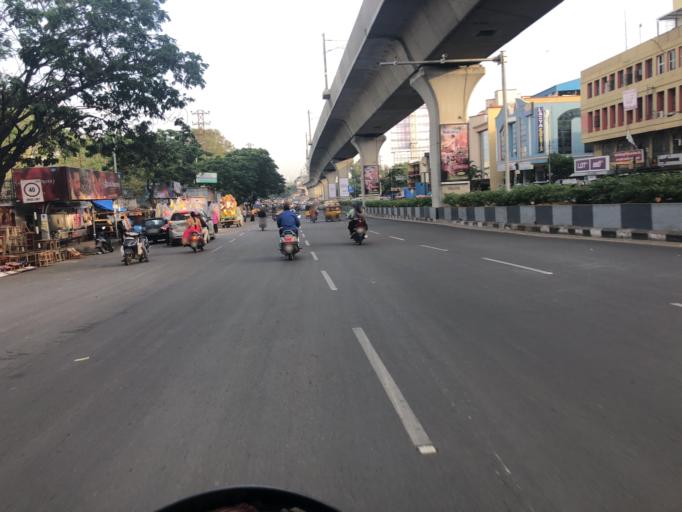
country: IN
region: Telangana
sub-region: Rangareddi
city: Kukatpalli
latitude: 17.4531
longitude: 78.4355
